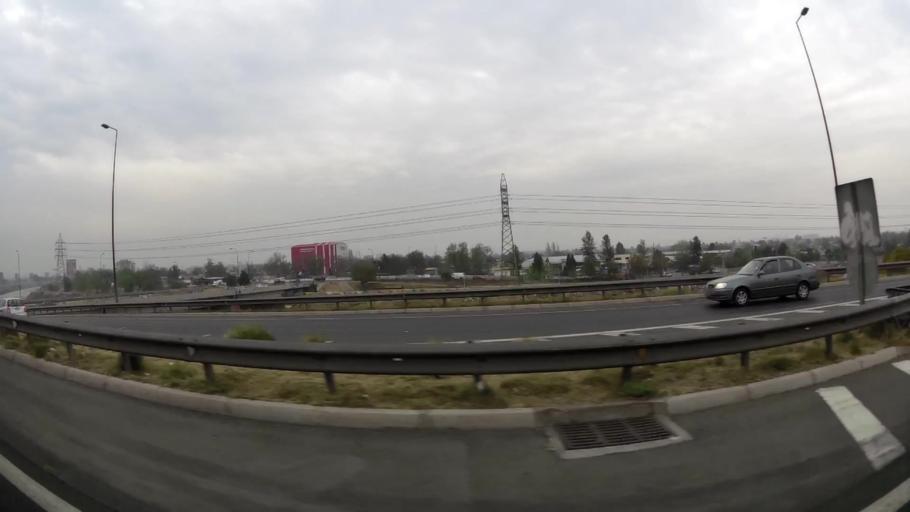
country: CL
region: Santiago Metropolitan
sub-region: Provincia de Santiago
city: Lo Prado
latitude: -33.4073
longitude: -70.7065
